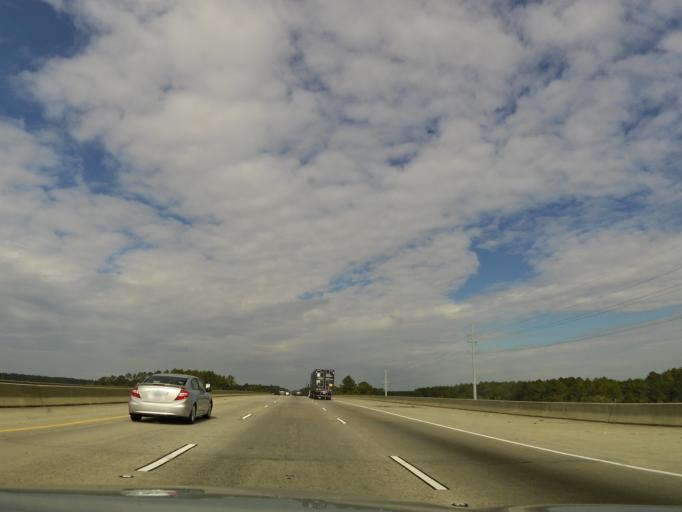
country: US
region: Georgia
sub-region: Liberty County
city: Midway
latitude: 31.8284
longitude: -81.3555
